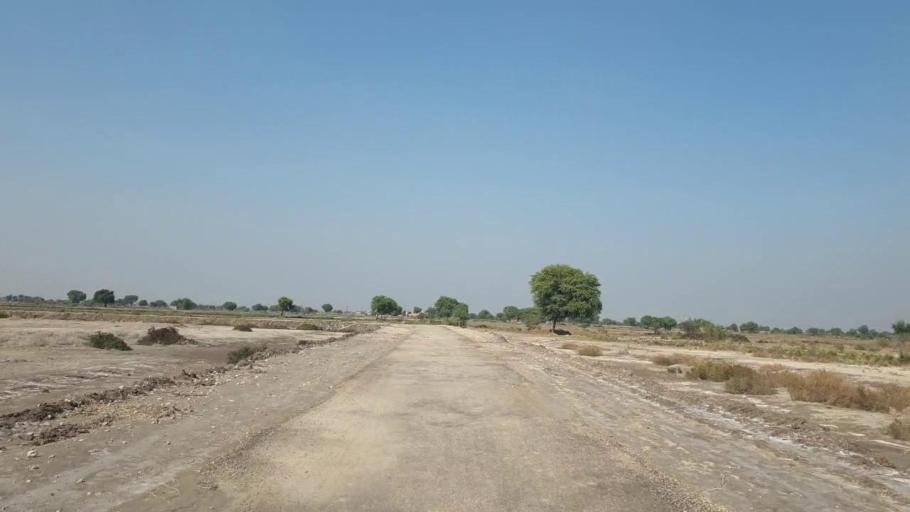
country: PK
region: Sindh
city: Sehwan
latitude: 26.4272
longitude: 67.8334
